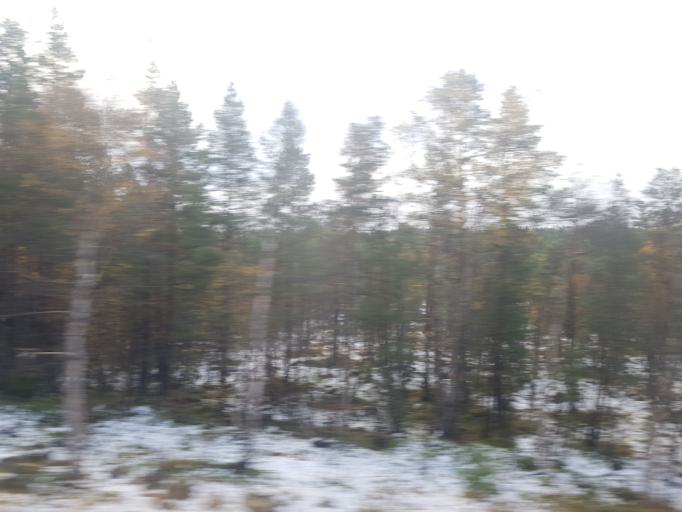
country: NO
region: Sor-Trondelag
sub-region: Oppdal
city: Oppdal
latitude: 62.6342
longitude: 9.7961
